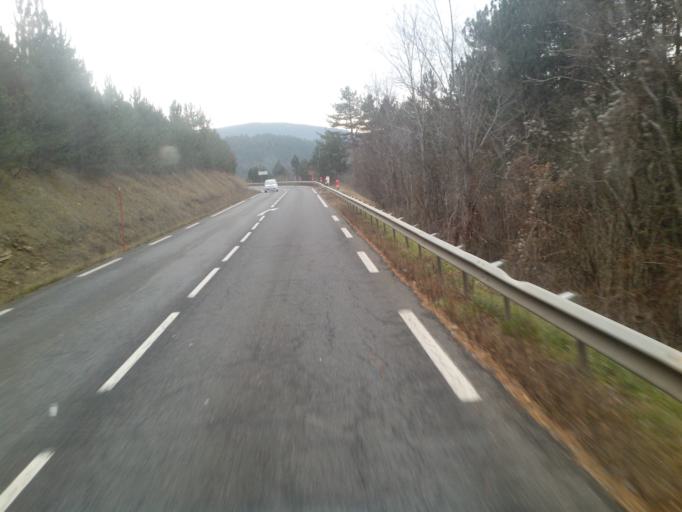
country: FR
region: Languedoc-Roussillon
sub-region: Departement de la Lozere
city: Mende
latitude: 44.5436
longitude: 3.5037
